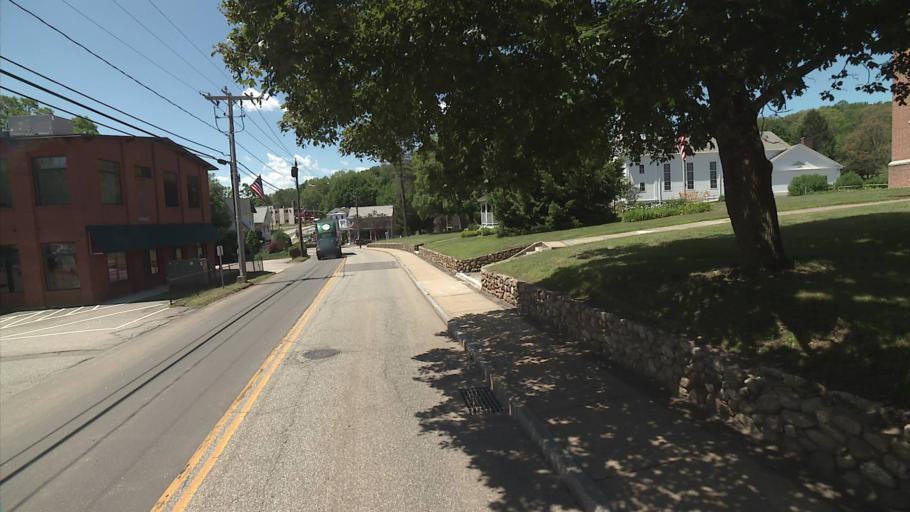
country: US
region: Connecticut
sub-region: Middlesex County
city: East Hampton
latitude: 41.5764
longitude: -72.5016
